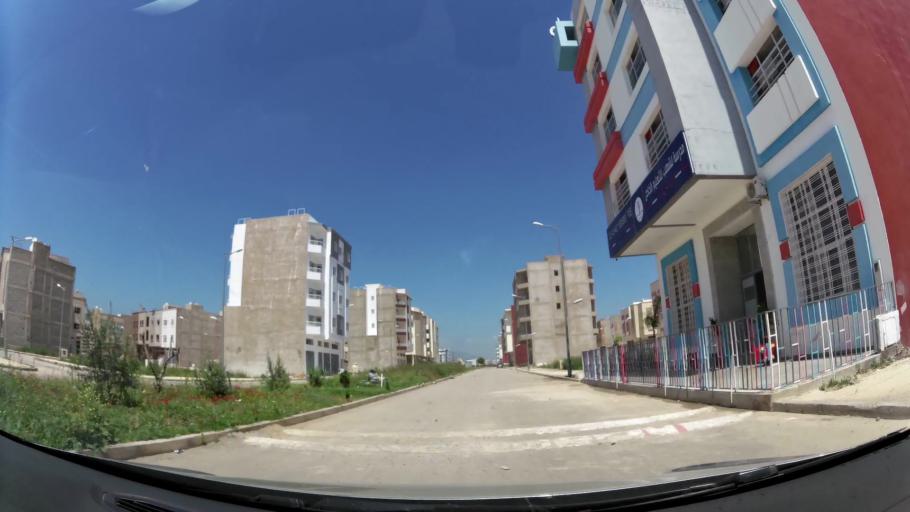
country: MA
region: Fes-Boulemane
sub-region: Fes
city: Fes
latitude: 34.0220
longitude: -5.0591
